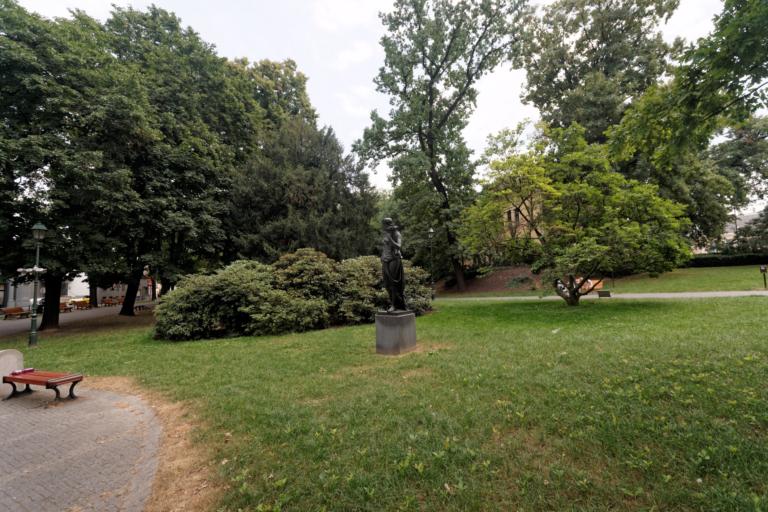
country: CZ
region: Moravskoslezsky
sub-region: Okres Opava
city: Opava
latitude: 49.9361
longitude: 17.9013
